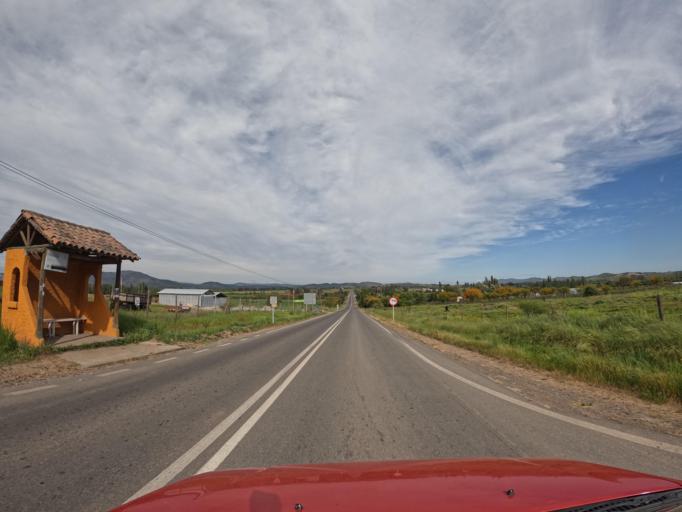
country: CL
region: Maule
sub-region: Provincia de Talca
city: Talca
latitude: -35.3748
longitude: -71.8366
